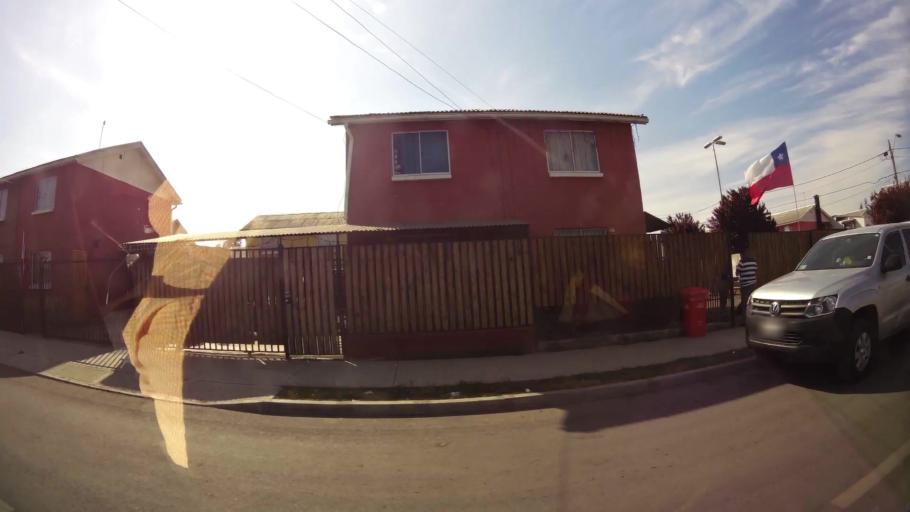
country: CL
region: Santiago Metropolitan
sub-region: Provincia de Talagante
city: El Monte
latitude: -33.6817
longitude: -70.9544
